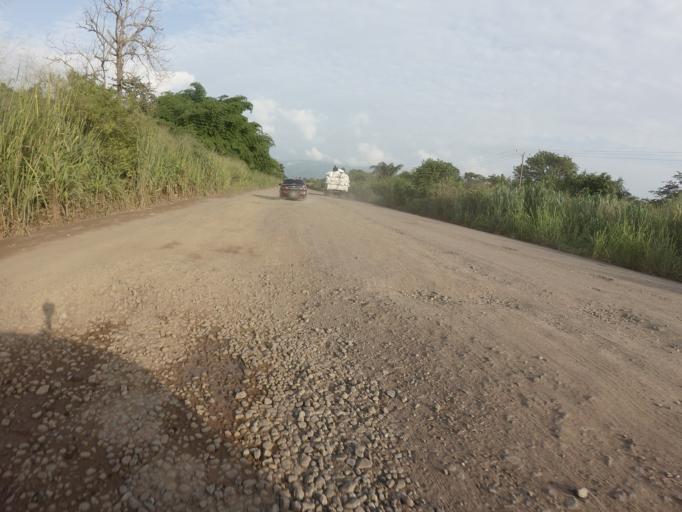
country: GH
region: Volta
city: Kpandu
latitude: 6.9738
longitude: 0.4513
